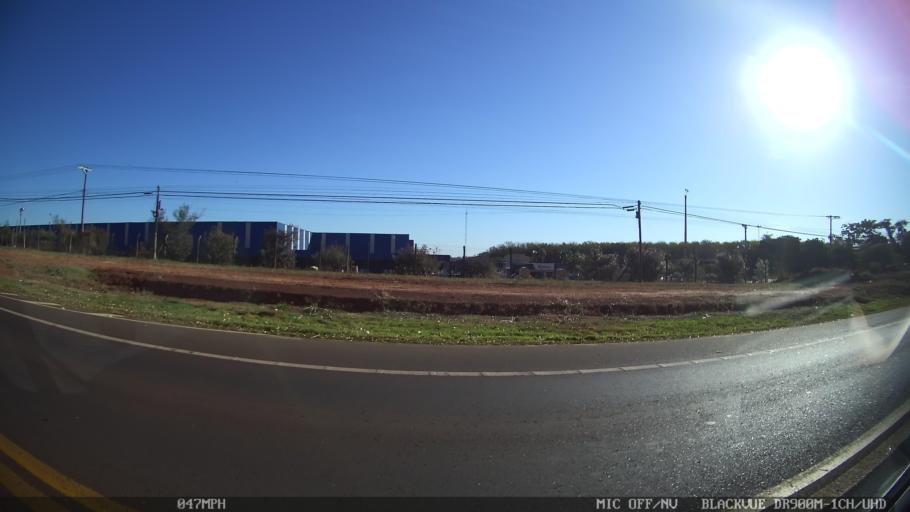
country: BR
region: Sao Paulo
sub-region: Olimpia
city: Olimpia
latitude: -20.7085
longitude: -48.9108
